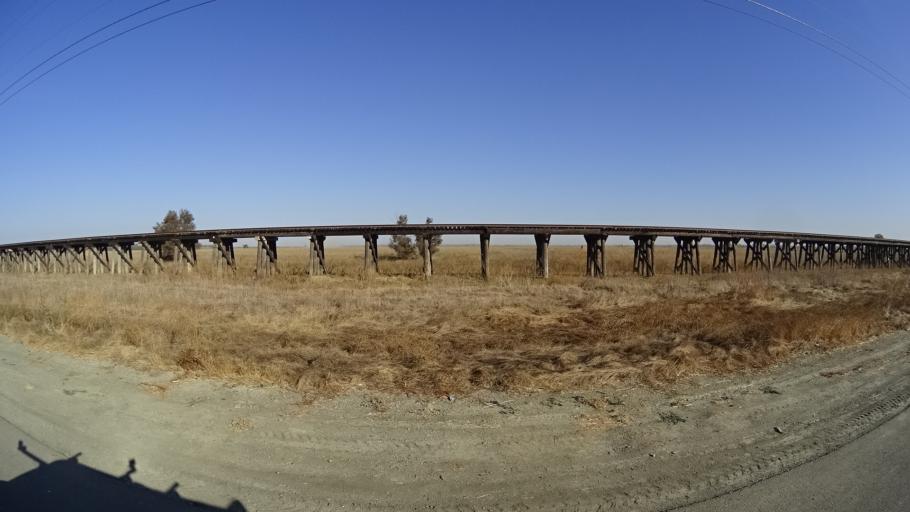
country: US
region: California
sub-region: Yolo County
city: Woodland
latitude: 38.6764
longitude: -121.6625
